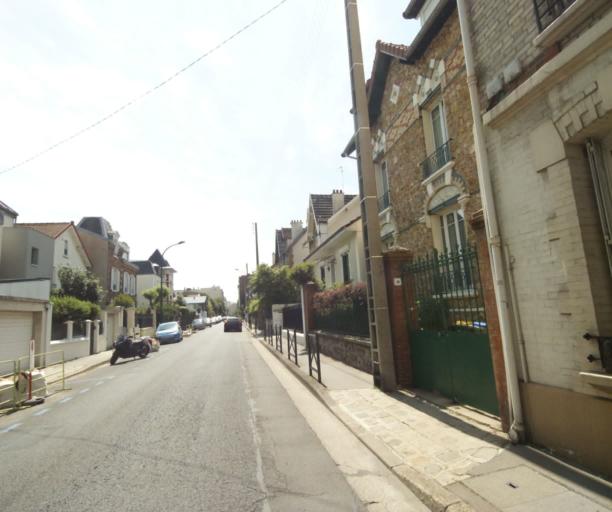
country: FR
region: Ile-de-France
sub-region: Departement des Hauts-de-Seine
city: Bois-Colombes
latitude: 48.9099
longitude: 2.2651
